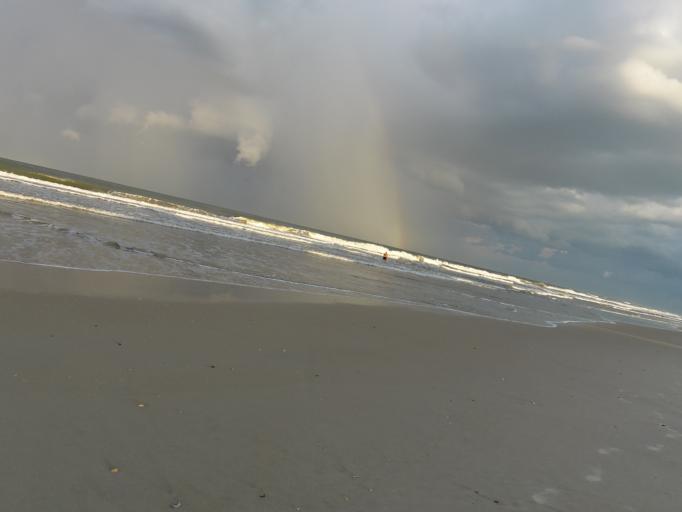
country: US
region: Florida
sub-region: Saint Johns County
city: Villano Beach
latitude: 29.9531
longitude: -81.3041
